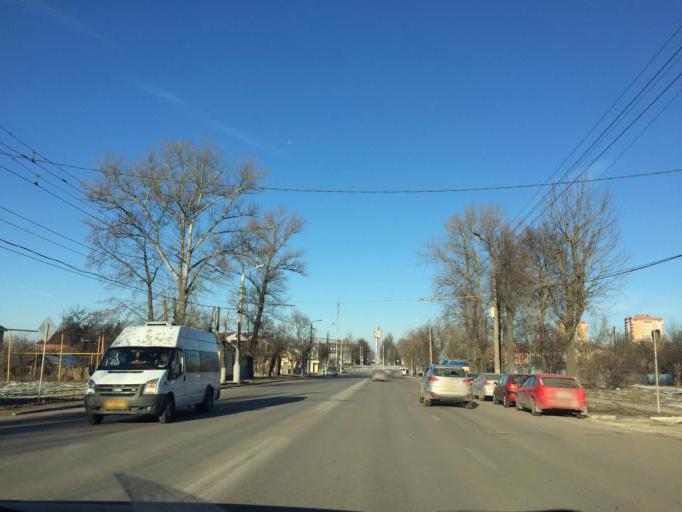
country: RU
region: Tula
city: Tula
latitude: 54.1833
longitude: 37.5727
